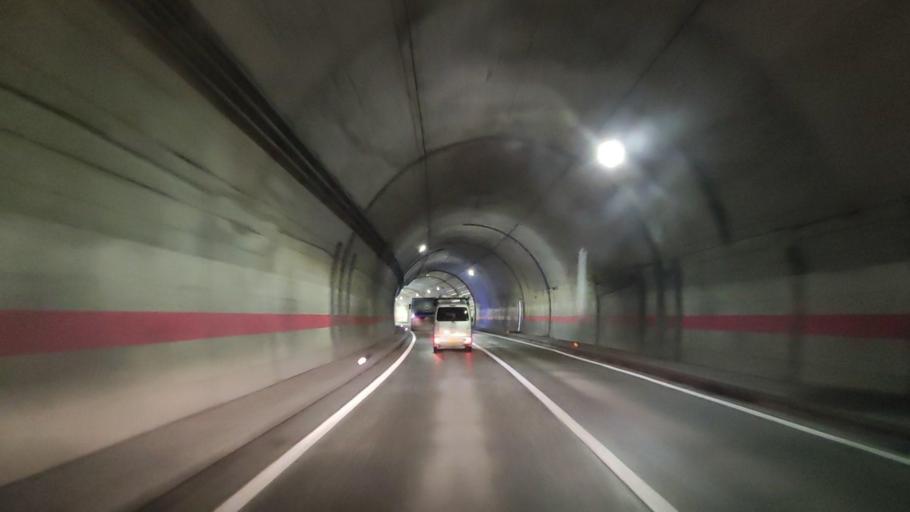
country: JP
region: Gifu
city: Takayama
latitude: 36.2559
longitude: 137.4741
